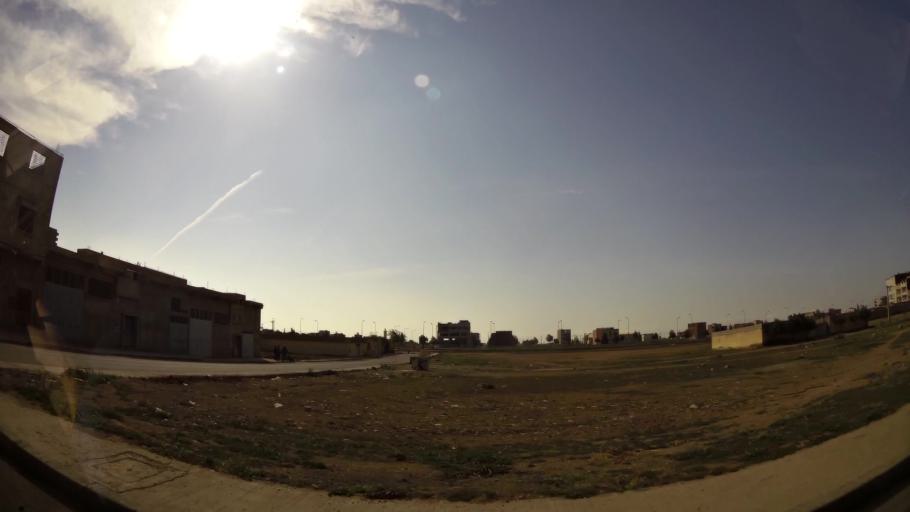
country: MA
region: Oriental
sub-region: Oujda-Angad
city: Oujda
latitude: 34.7130
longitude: -1.8839
